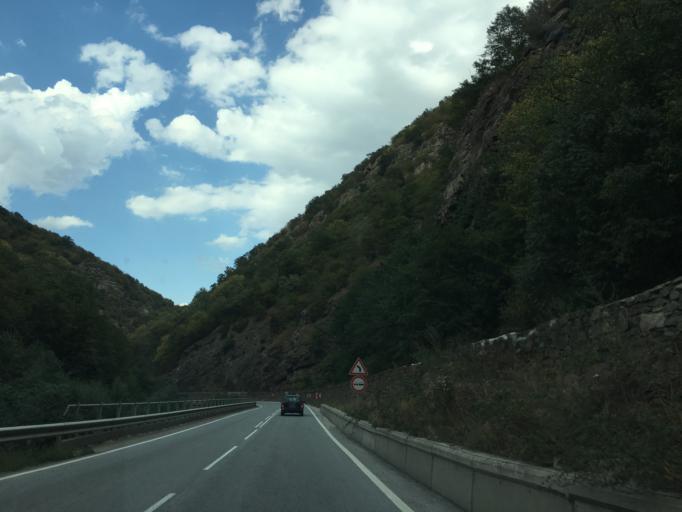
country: BG
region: Pazardzhik
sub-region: Obshtina Septemvri
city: Septemvri
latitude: 42.1140
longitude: 24.1149
